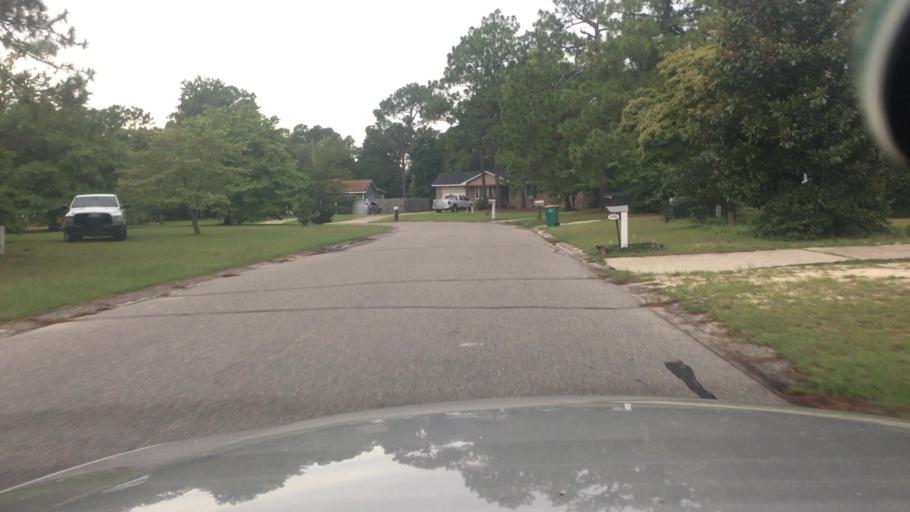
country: US
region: North Carolina
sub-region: Cumberland County
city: Hope Mills
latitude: 34.9728
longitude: -78.9743
